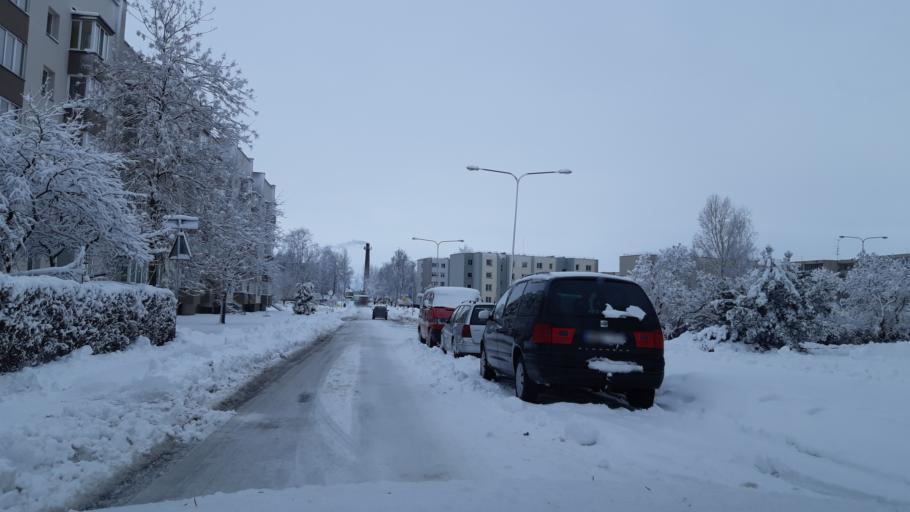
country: LT
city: Kybartai
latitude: 54.6365
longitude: 22.7564
